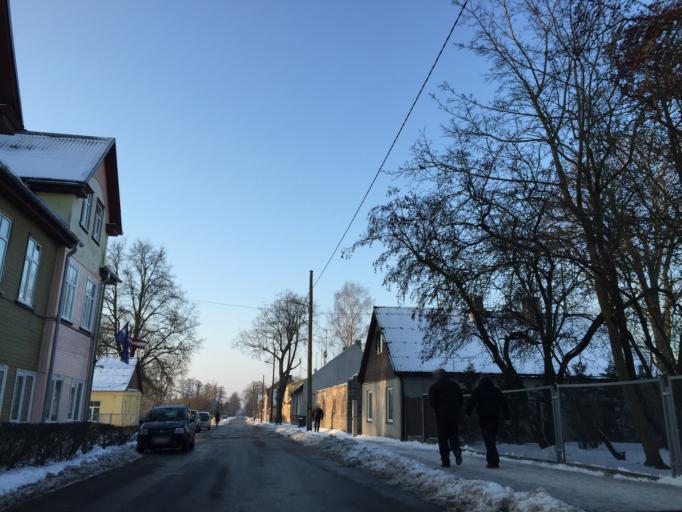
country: LV
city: Tireli
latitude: 56.9417
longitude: 23.6187
